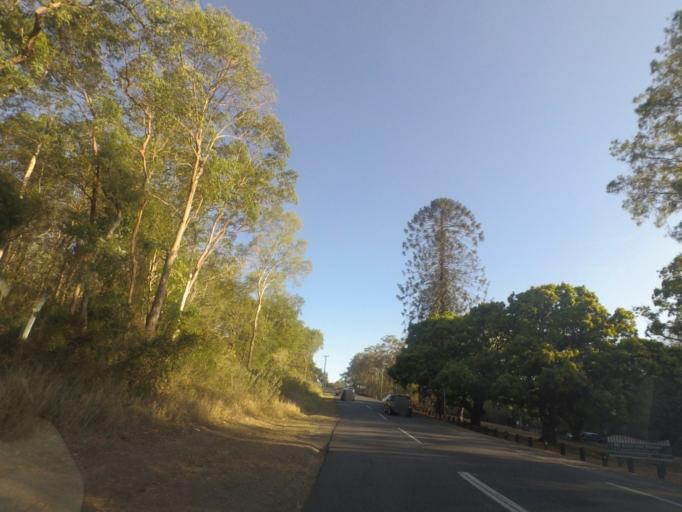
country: AU
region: Queensland
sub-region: Brisbane
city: Taringa
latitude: -27.4700
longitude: 152.9711
